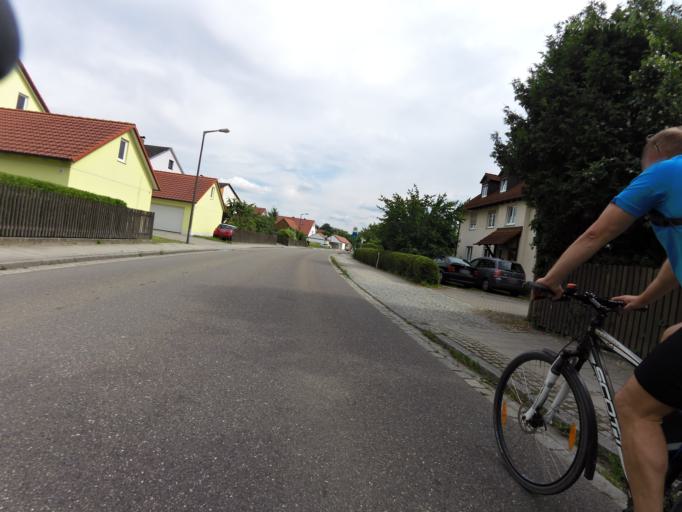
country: DE
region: Bavaria
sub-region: Upper Bavaria
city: Hebertshausen
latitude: 48.3012
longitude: 11.4922
